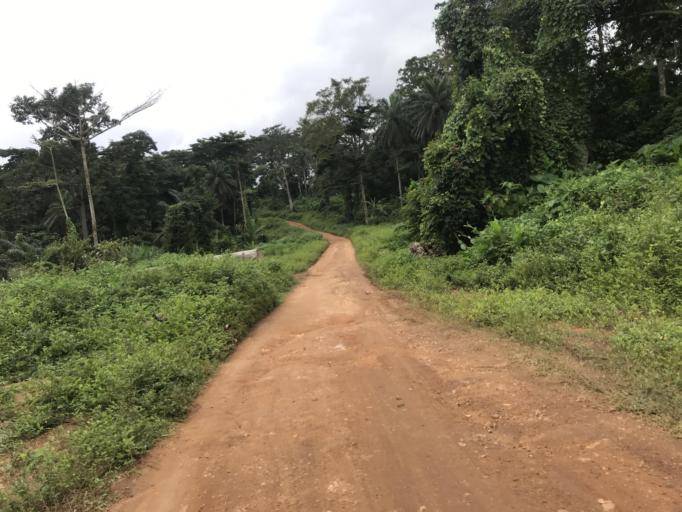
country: SL
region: Eastern Province
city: Buedu
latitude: 8.3943
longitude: -10.3983
